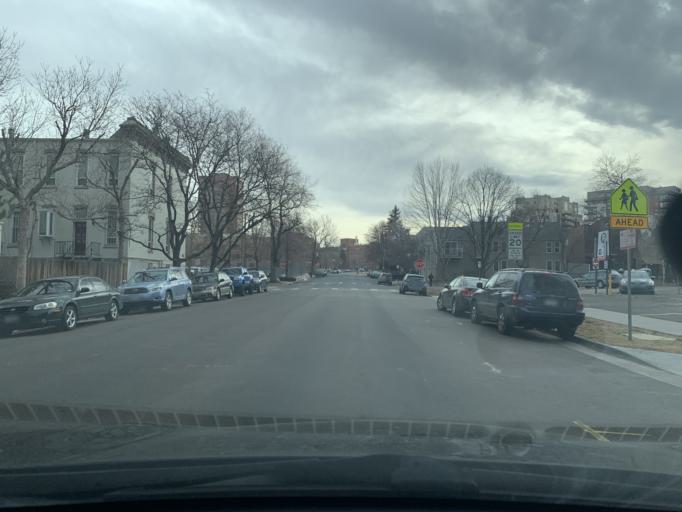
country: US
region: Colorado
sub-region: Denver County
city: Denver
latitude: 39.7498
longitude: -104.9837
